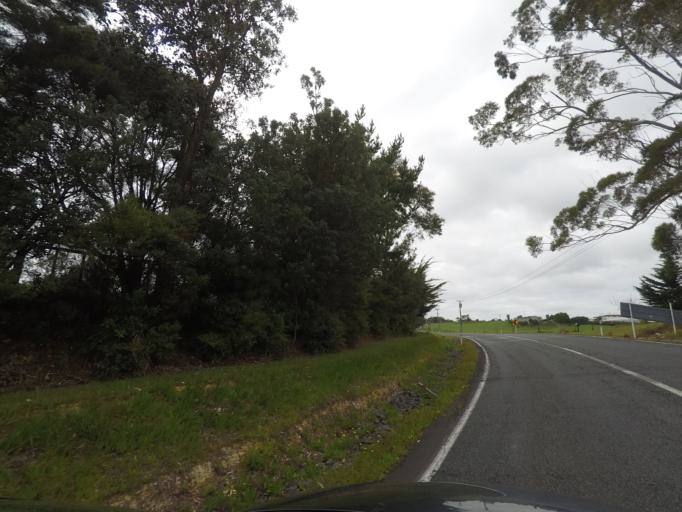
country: NZ
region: Auckland
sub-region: Auckland
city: Rosebank
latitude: -36.8355
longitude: 174.5782
